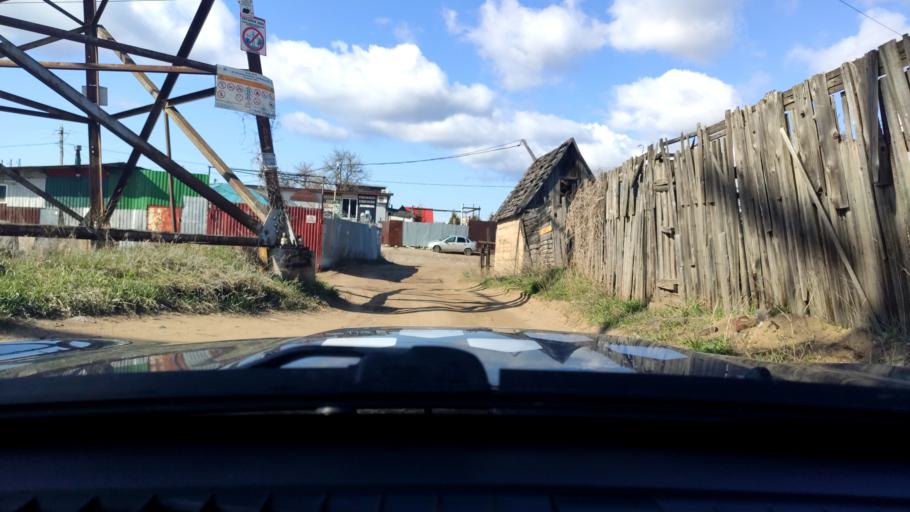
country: RU
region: Samara
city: Zhigulevsk
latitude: 53.4956
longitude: 49.4980
